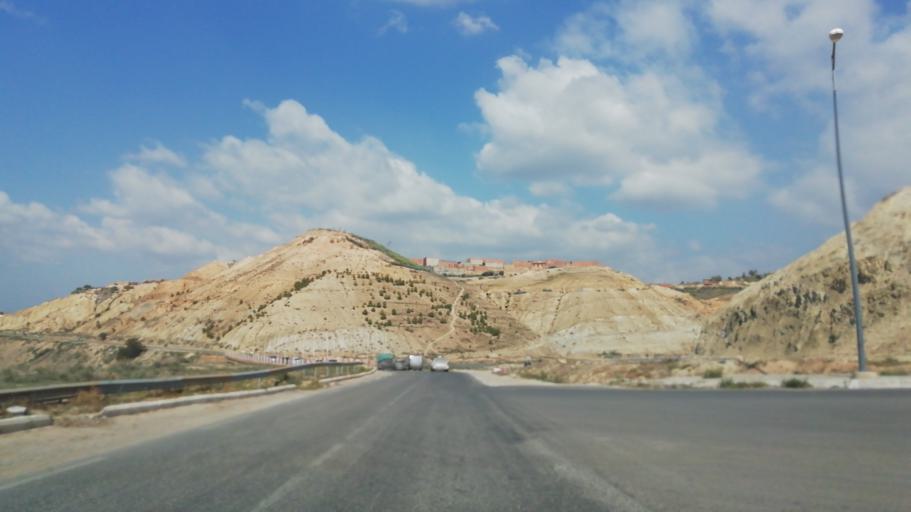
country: DZ
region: Mascara
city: Mascara
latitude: 35.5644
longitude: 0.0719
